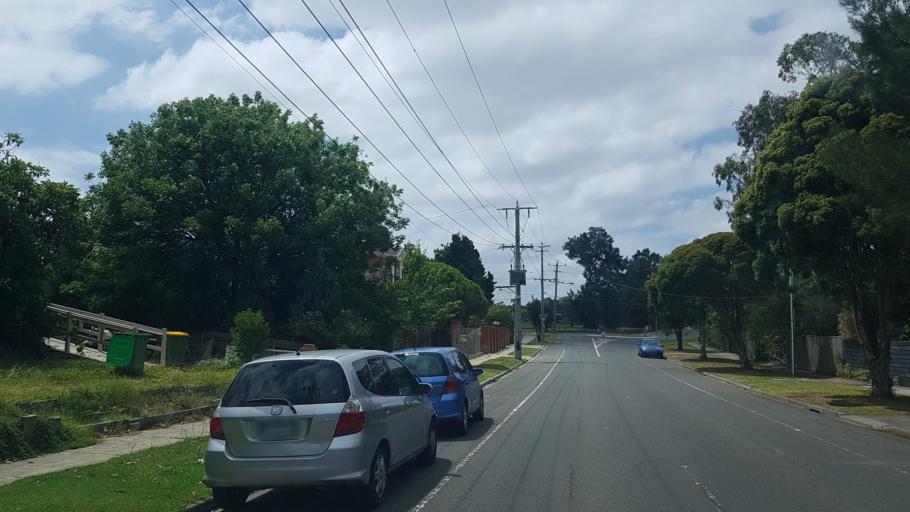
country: AU
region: Victoria
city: Rosanna
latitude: -37.7485
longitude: 145.0686
